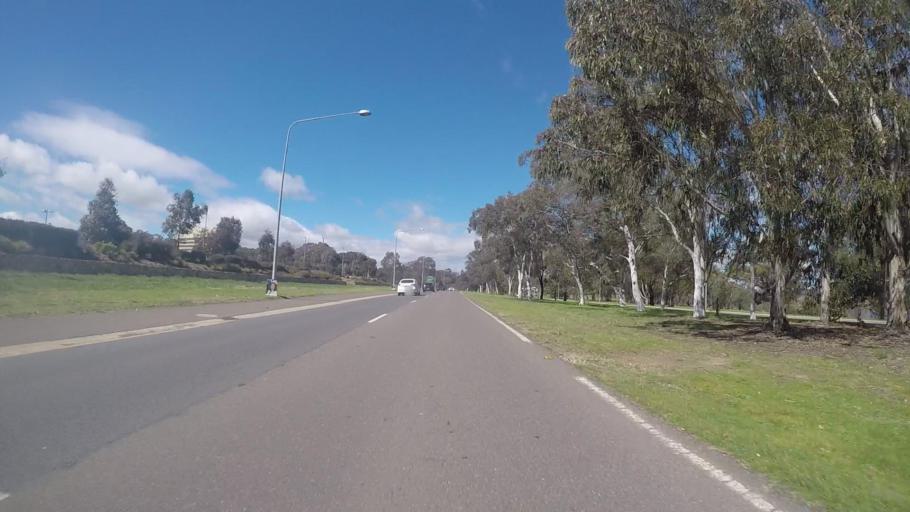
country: AU
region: Australian Capital Territory
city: Canberra
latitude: -35.2937
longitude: 149.1441
